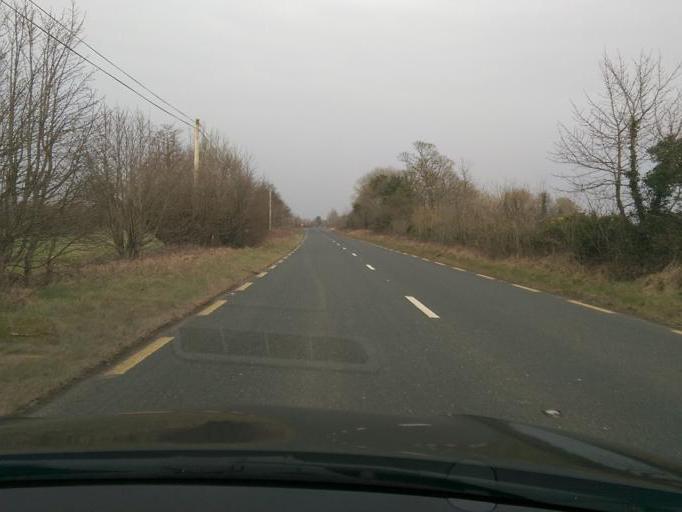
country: IE
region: Connaught
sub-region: Roscommon
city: Roscommon
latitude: 53.6540
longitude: -8.1046
